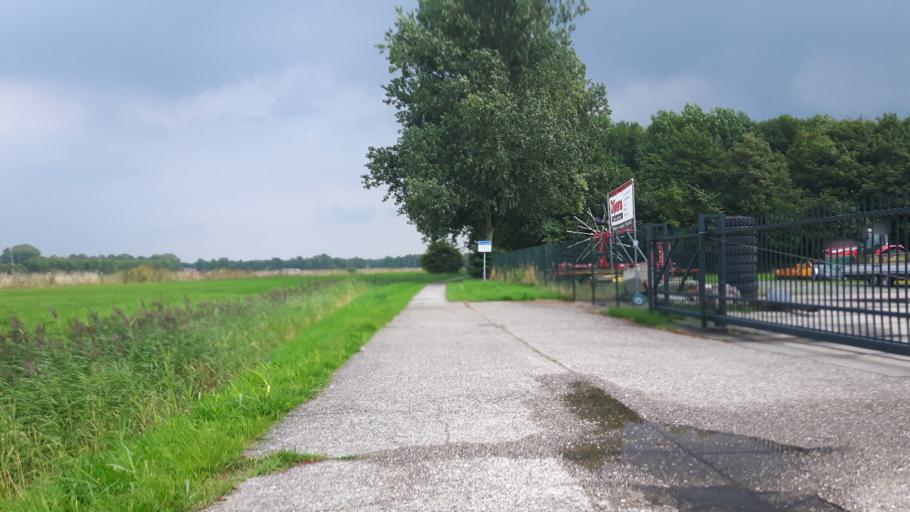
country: NL
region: Groningen
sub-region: Gemeente Bedum
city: Bedum
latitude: 53.3397
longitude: 6.6374
